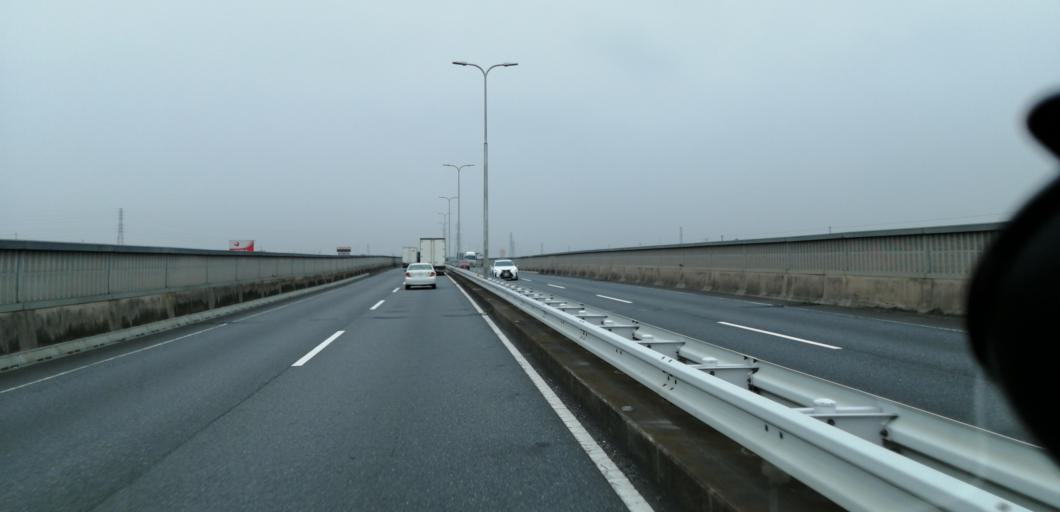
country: JP
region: Saitama
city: Kumagaya
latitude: 36.1656
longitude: 139.3887
